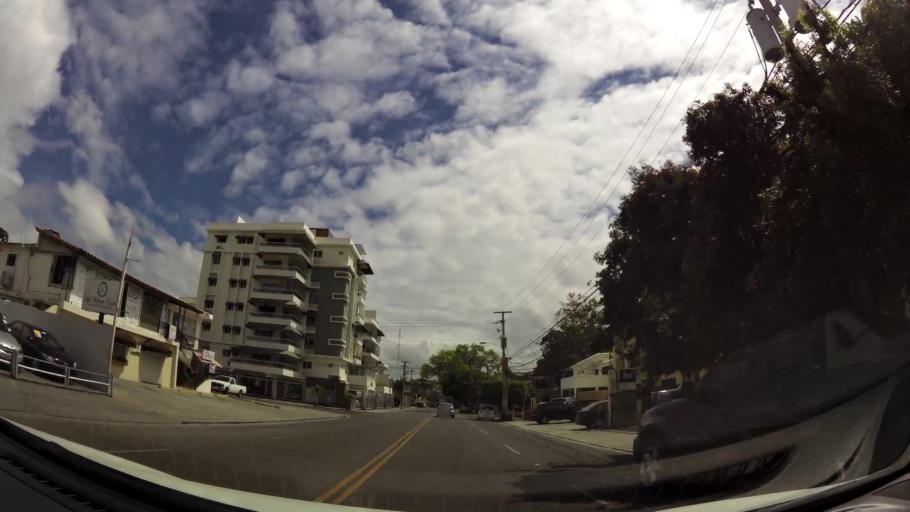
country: DO
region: Nacional
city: Bella Vista
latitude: 18.4714
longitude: -69.9590
